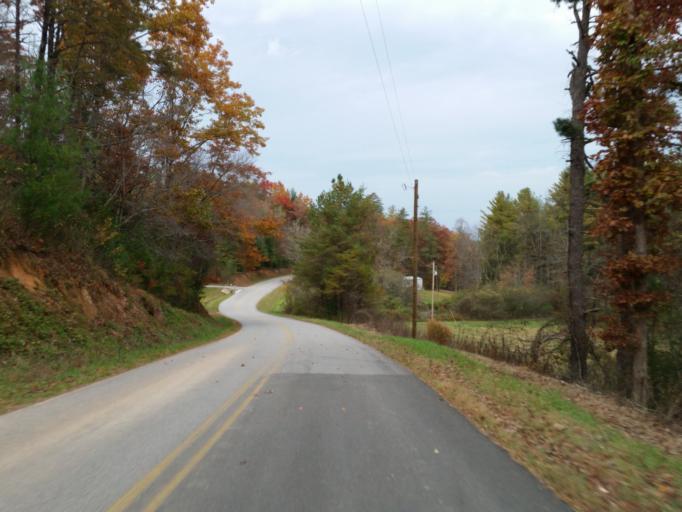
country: US
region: Georgia
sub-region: Fannin County
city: Blue Ridge
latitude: 34.7345
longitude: -84.1962
